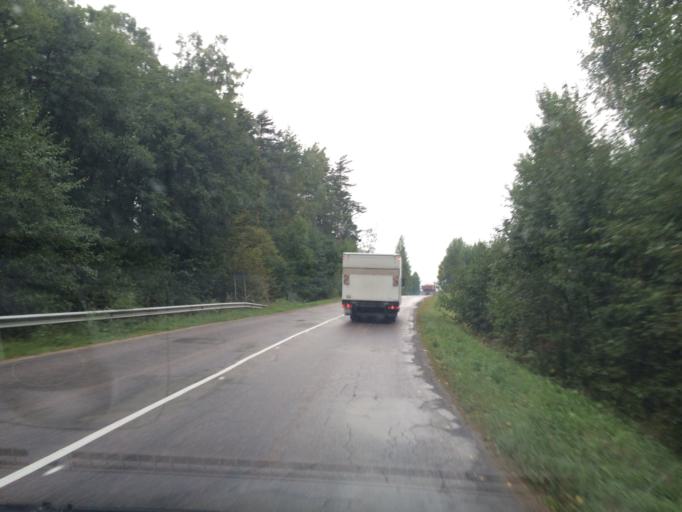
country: LV
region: Ikskile
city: Ikskile
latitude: 56.8548
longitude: 24.5346
